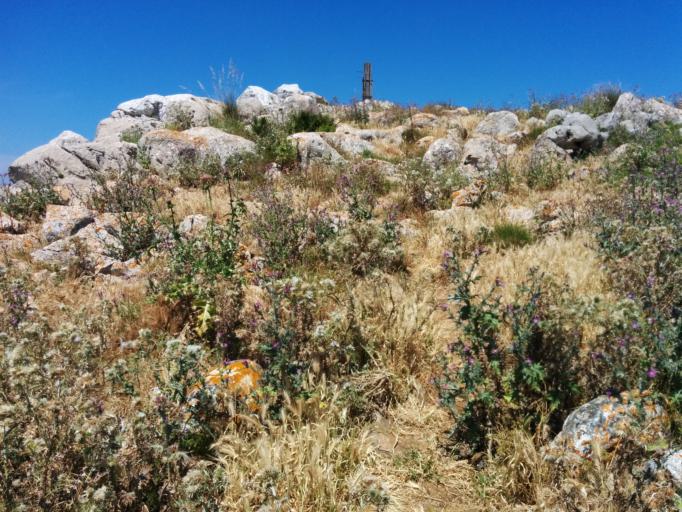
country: IT
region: Sicily
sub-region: Trapani
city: San Vito Lo Capo
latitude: 38.1669
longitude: 12.7572
